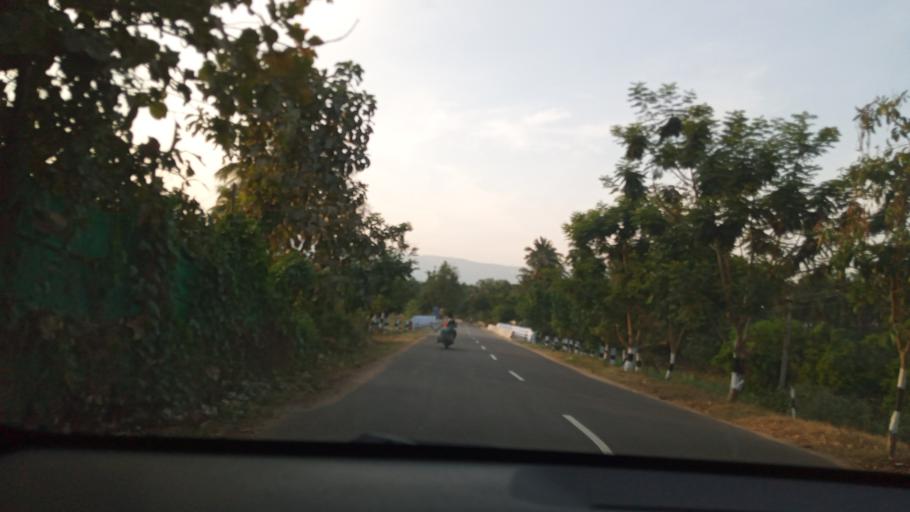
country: IN
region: Tamil Nadu
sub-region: Coimbatore
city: Perur
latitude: 10.9477
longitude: 76.7698
